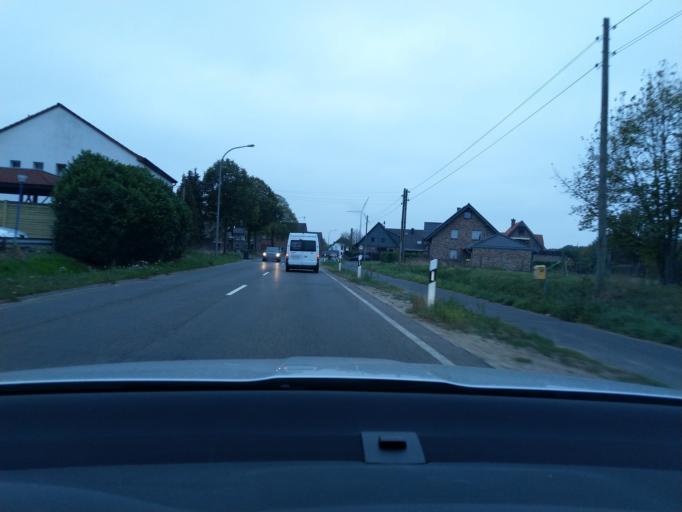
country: DE
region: North Rhine-Westphalia
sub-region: Regierungsbezirk Dusseldorf
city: Schwalmtal
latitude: 51.2324
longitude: 6.3071
